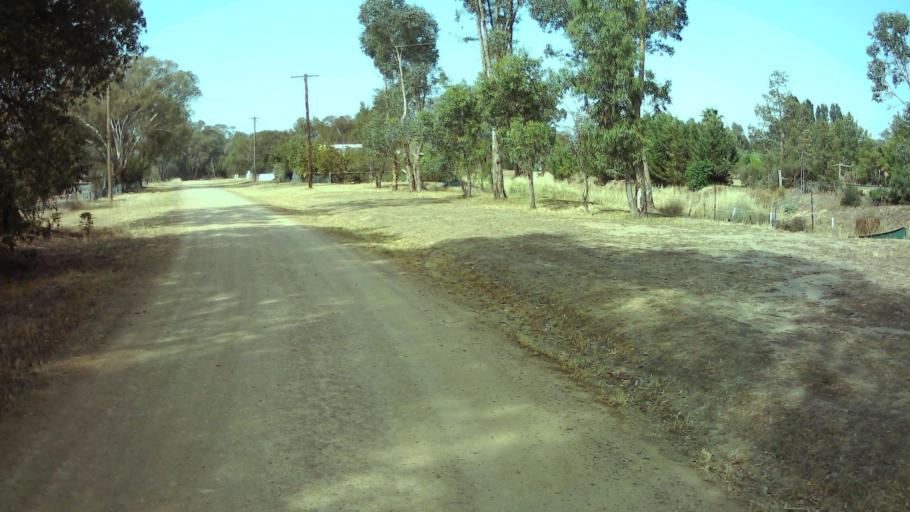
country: AU
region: New South Wales
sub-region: Weddin
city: Grenfell
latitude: -33.8967
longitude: 148.1525
